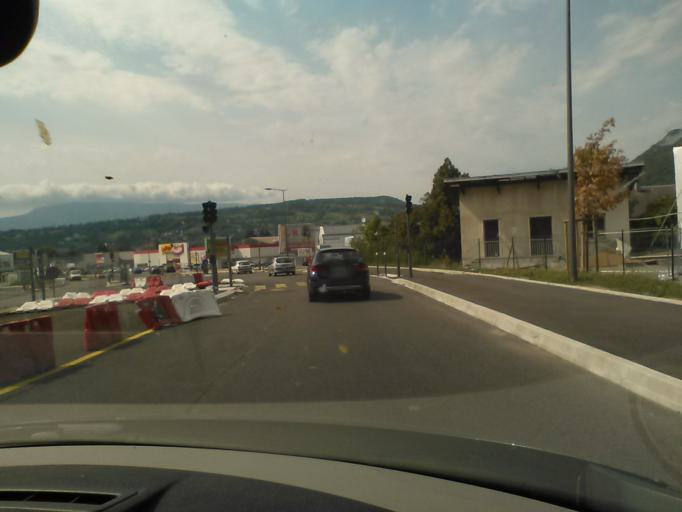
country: FR
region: Rhone-Alpes
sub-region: Departement de la Savoie
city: Saint-Alban-Leysse
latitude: 45.5729
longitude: 5.9585
